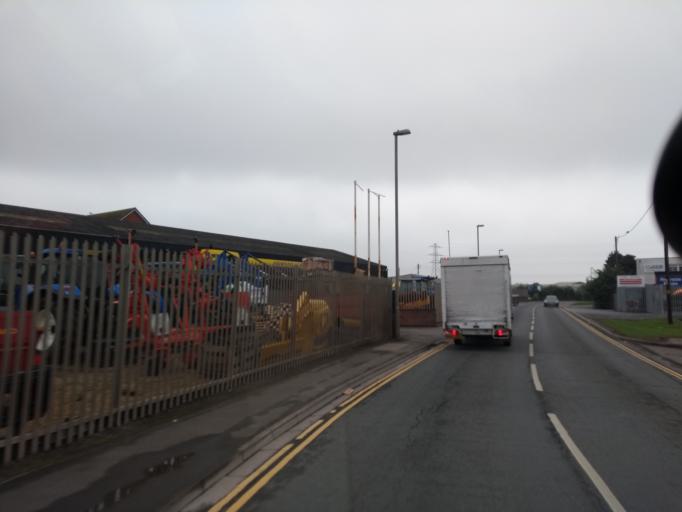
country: GB
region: England
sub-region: Somerset
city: Bridgwater
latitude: 51.1237
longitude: -2.9933
